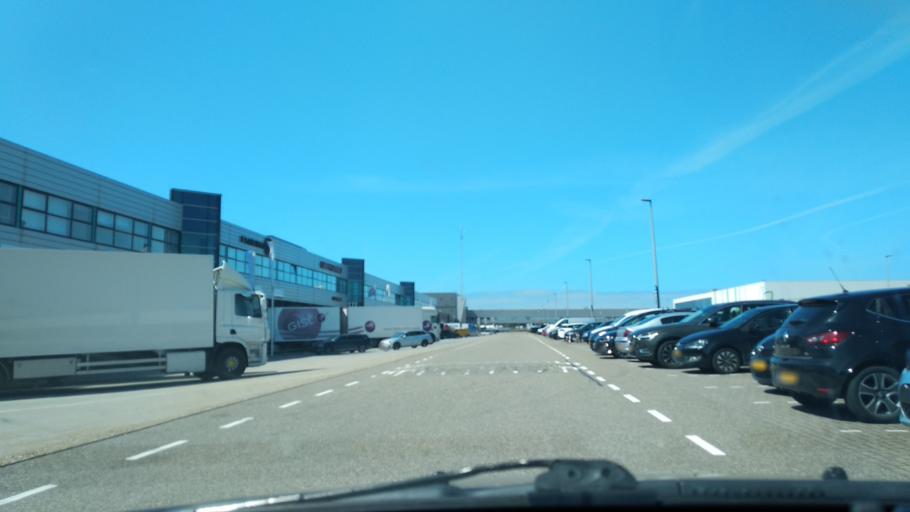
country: NL
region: South Holland
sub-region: Gemeente Westland
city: Honselersdijk
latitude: 51.9949
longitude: 4.2361
